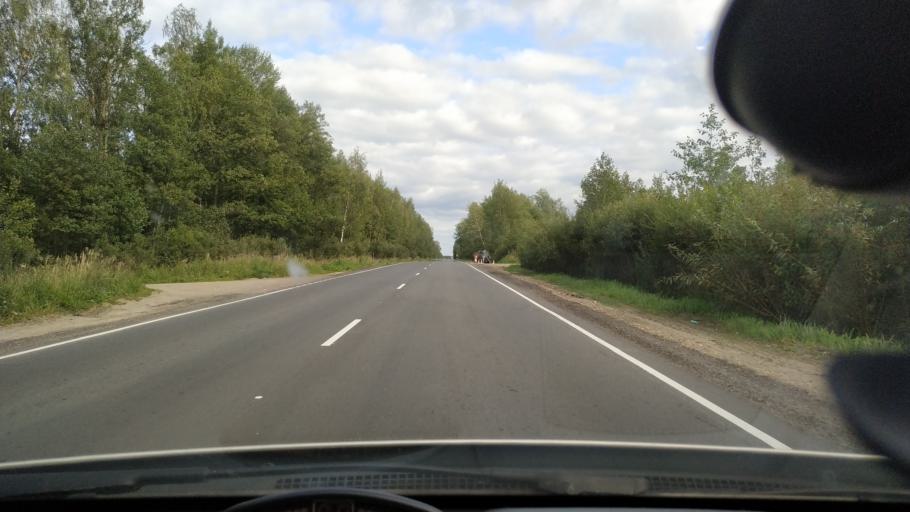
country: RU
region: Moskovskaya
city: Likino-Dulevo
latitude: 55.7275
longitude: 39.0299
